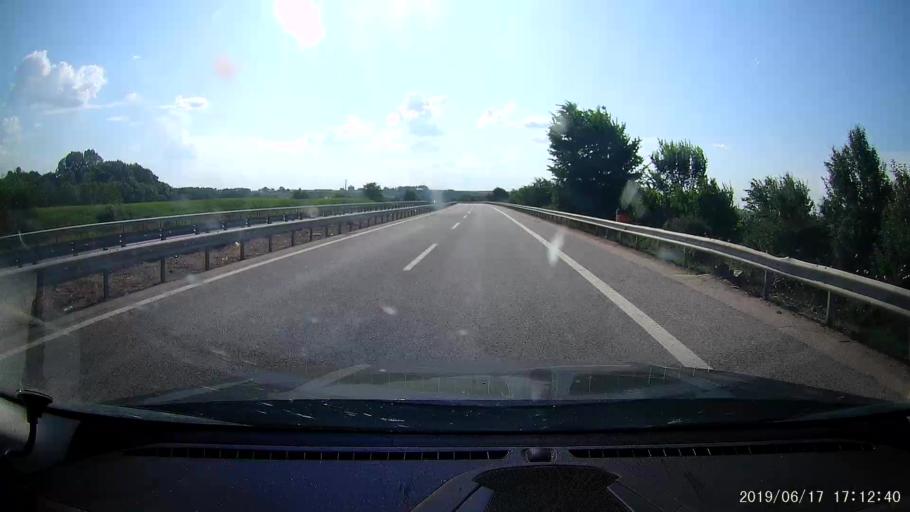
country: TR
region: Edirne
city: Edirne
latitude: 41.7007
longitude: 26.5577
